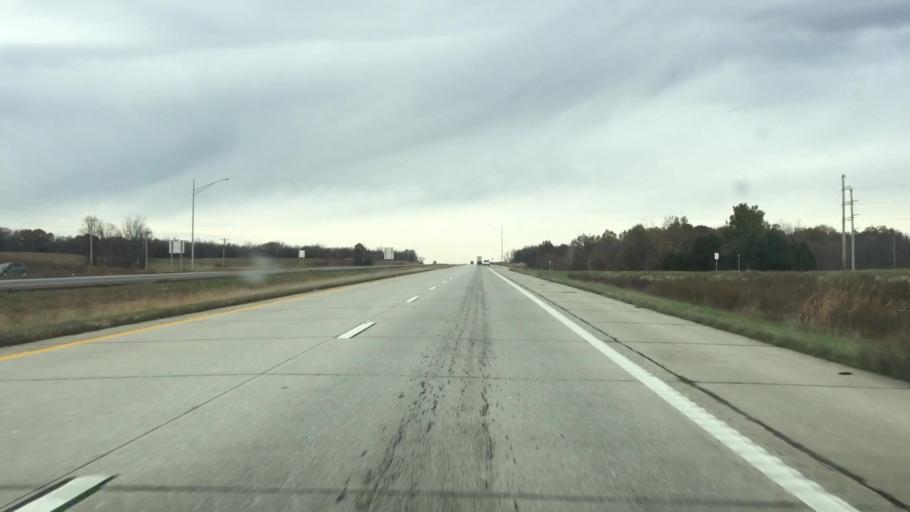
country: US
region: Missouri
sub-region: Saint Clair County
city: Osceola
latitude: 38.0417
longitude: -93.6819
